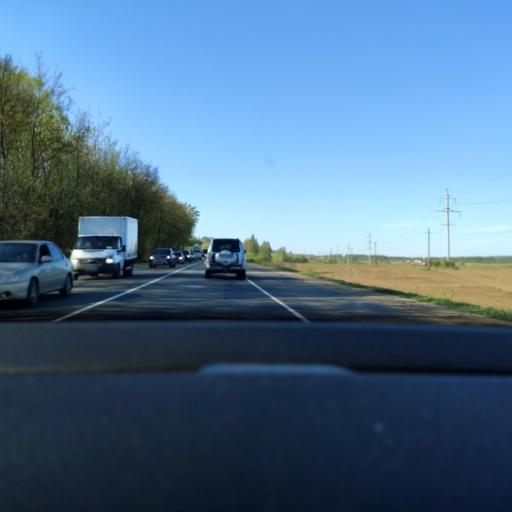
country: RU
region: Moskovskaya
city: Yakhroma
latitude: 56.3289
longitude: 37.4825
